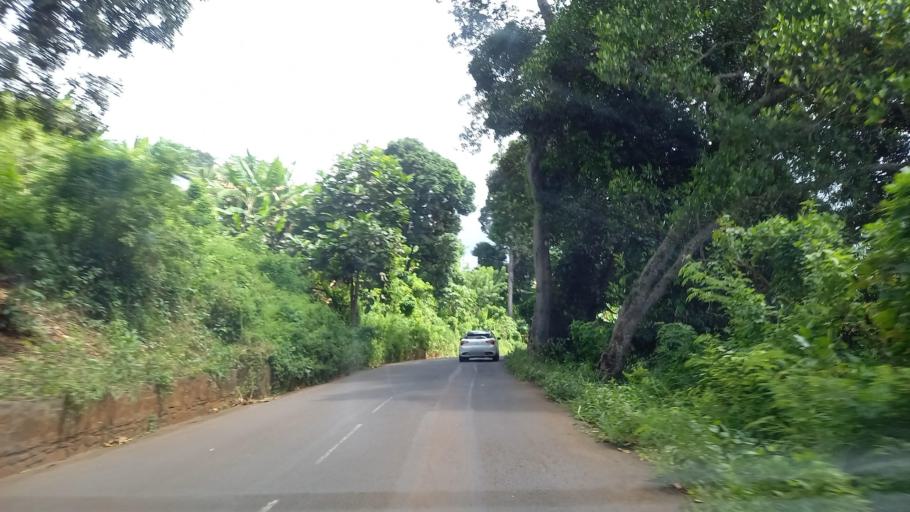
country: YT
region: Mamoudzou
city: Mamoudzou
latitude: -12.7919
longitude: 45.1822
